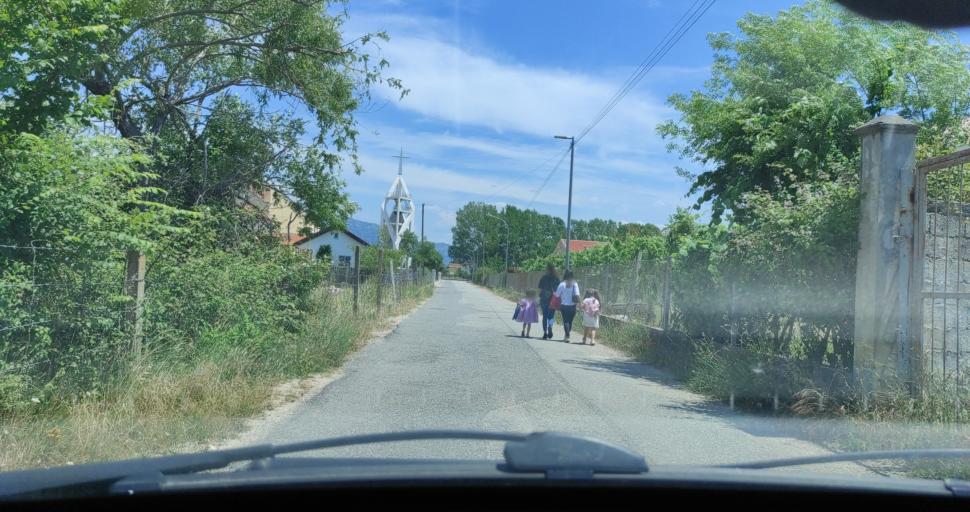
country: AL
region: Shkoder
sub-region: Rrethi i Shkodres
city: Velipoje
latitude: 41.8729
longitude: 19.4015
